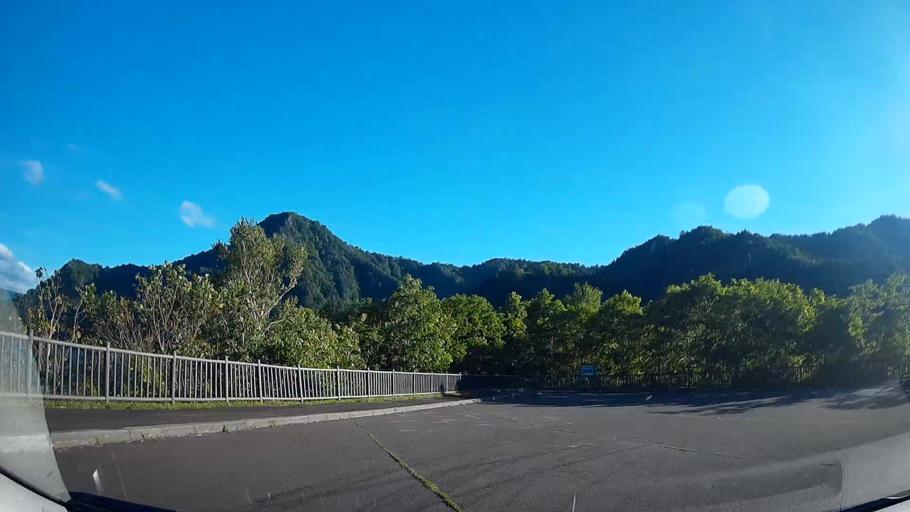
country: JP
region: Hokkaido
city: Sapporo
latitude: 43.0000
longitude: 141.1513
